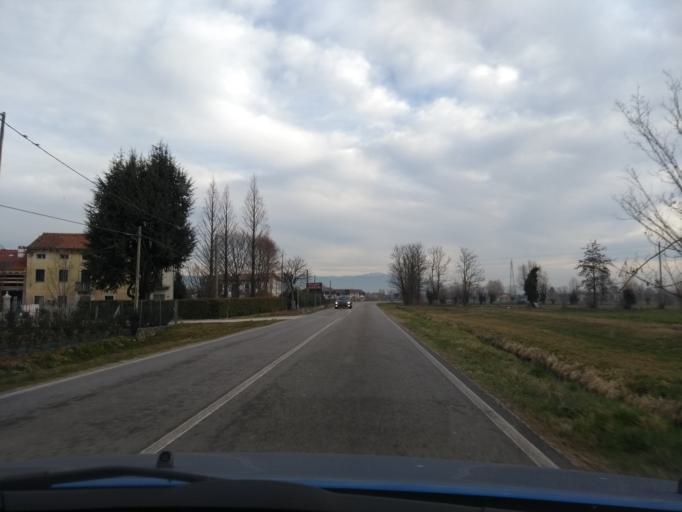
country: IT
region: Veneto
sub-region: Provincia di Vicenza
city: Bolzano Vicentino
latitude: 45.6061
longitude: 11.6453
